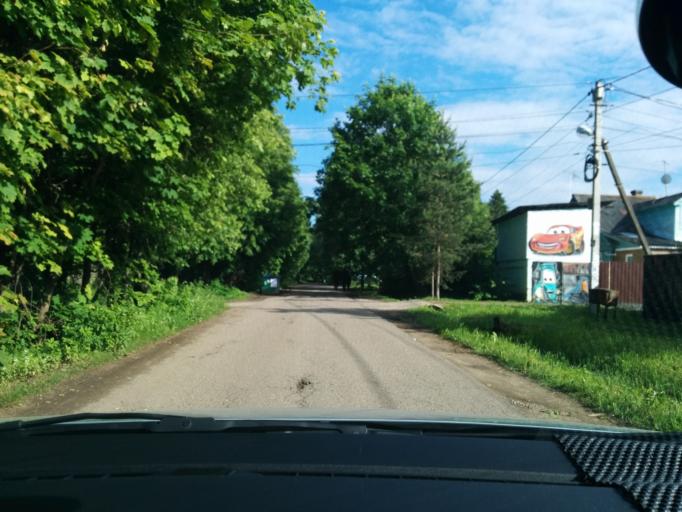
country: RU
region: Moskovskaya
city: Lugovaya
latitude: 56.0521
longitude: 37.4877
